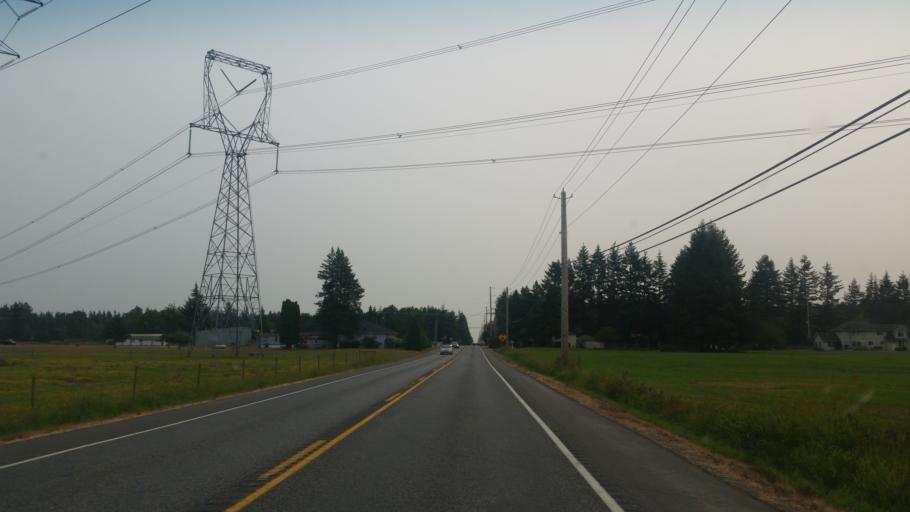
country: US
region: Washington
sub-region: Whatcom County
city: Ferndale
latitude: 48.8940
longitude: -122.5837
